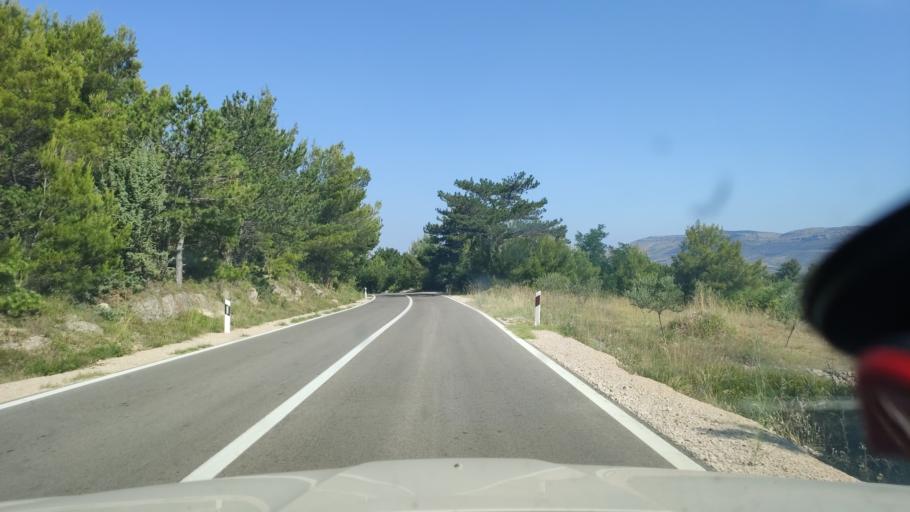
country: HR
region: Sibensko-Kniniska
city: Zaton
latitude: 43.9186
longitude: 15.8244
